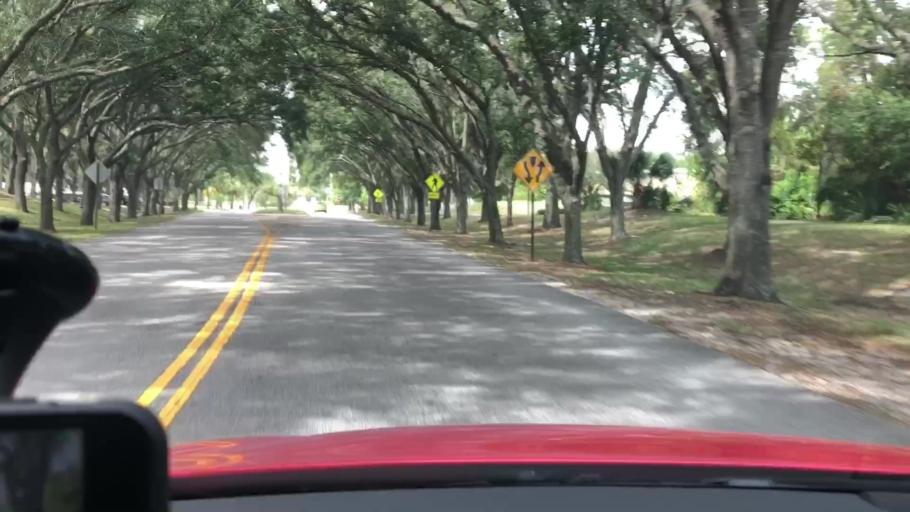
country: US
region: Florida
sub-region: Volusia County
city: Port Orange
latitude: 29.1255
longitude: -81.0185
